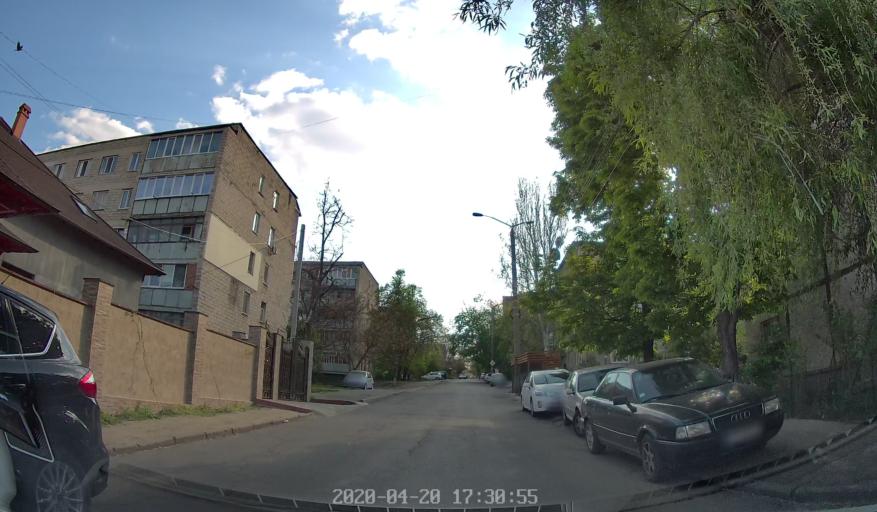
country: MD
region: Chisinau
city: Chisinau
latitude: 46.9985
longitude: 28.8697
